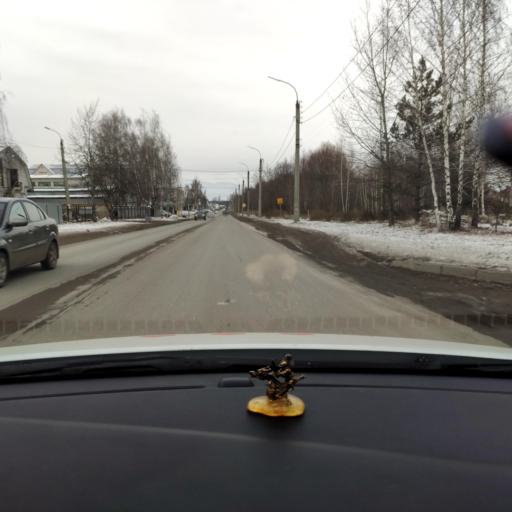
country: RU
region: Tatarstan
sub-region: Zelenodol'skiy Rayon
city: Zelenodolsk
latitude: 55.8628
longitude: 48.5498
